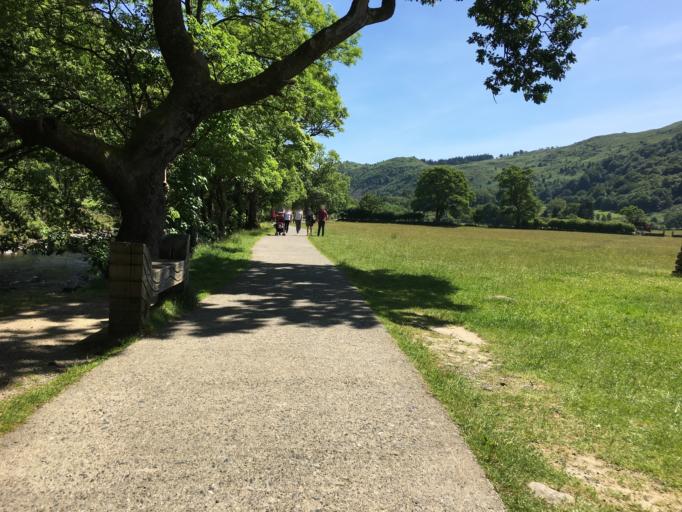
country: GB
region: Wales
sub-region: Gwynedd
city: Penrhyndeudraeth
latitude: 53.0110
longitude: -4.1011
